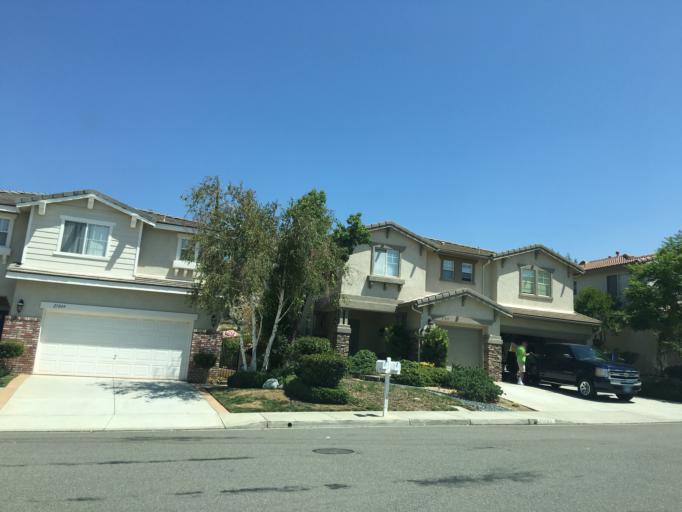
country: US
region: California
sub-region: Los Angeles County
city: Castaic
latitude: 34.5068
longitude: -118.6240
